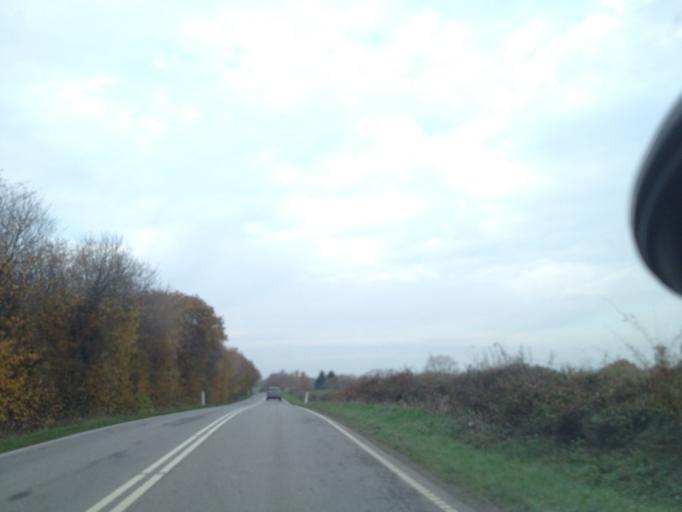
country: DK
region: South Denmark
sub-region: Assens Kommune
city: Vissenbjerg
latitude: 55.4522
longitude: 10.1217
